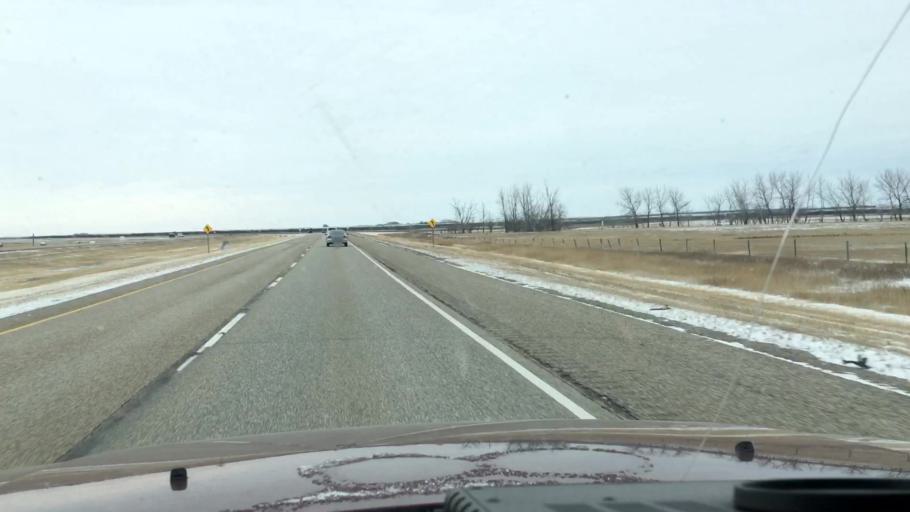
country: CA
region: Saskatchewan
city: Saskatoon
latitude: 51.4788
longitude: -106.2501
